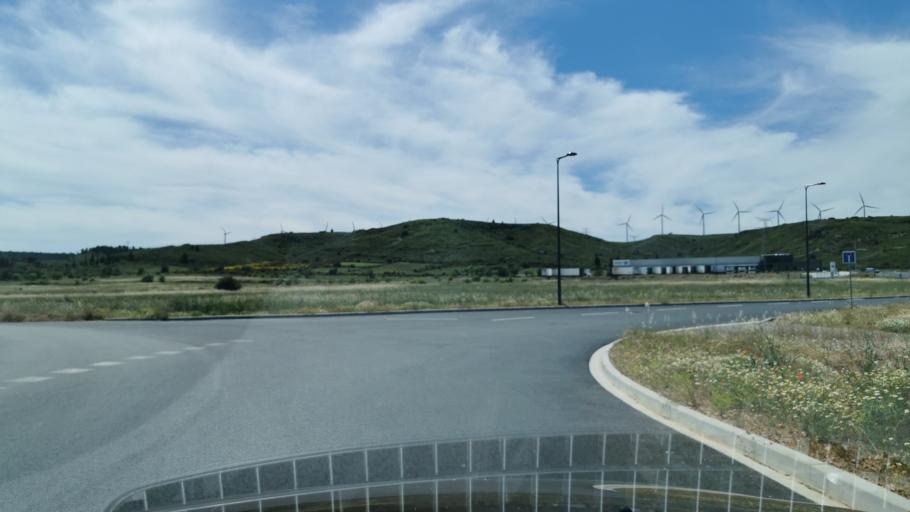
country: FR
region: Languedoc-Roussillon
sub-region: Departement de l'Aude
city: Nevian
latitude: 43.1965
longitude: 2.8973
